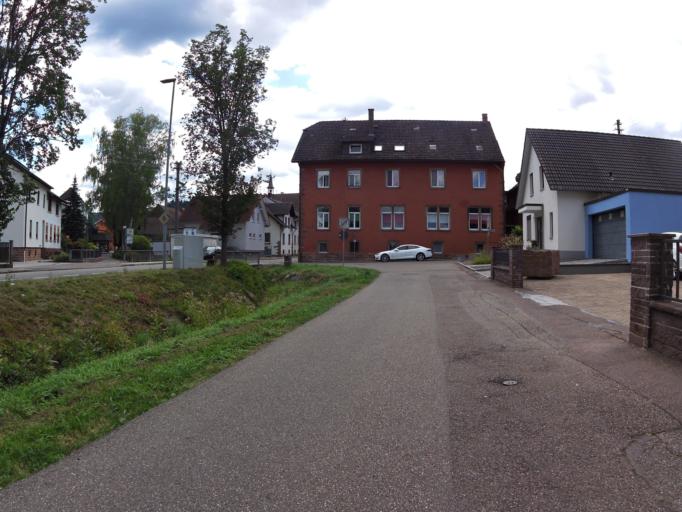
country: DE
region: Baden-Wuerttemberg
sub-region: Freiburg Region
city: Lahr
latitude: 48.3119
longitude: 7.8606
